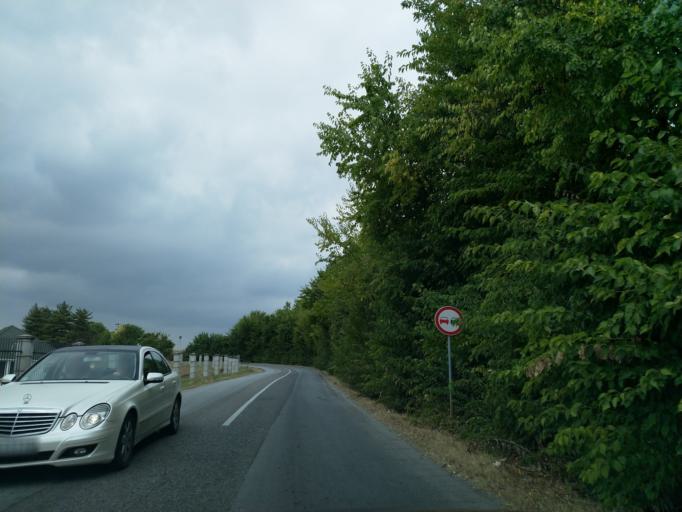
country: RS
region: Central Serbia
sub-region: Pomoravski Okrug
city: Jagodina
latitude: 43.9908
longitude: 21.2313
